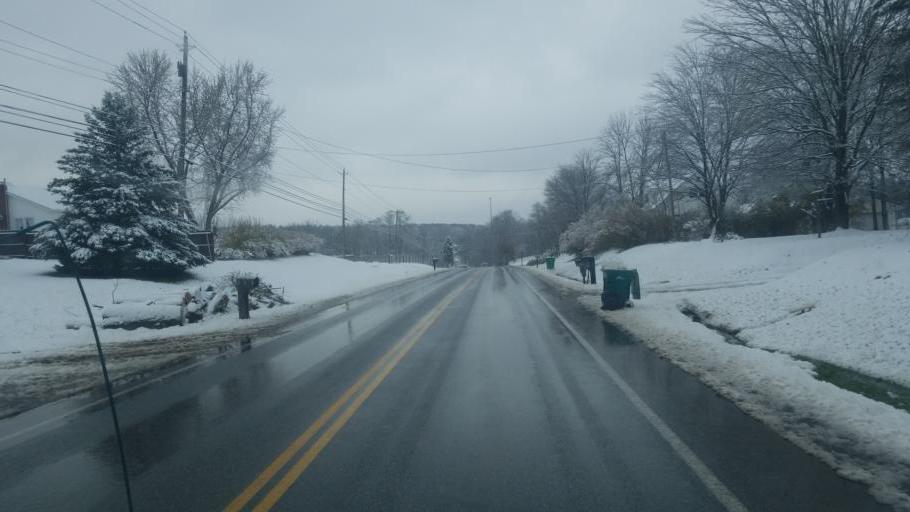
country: US
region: Ohio
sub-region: Portage County
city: Garrettsville
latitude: 41.3664
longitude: -81.0704
